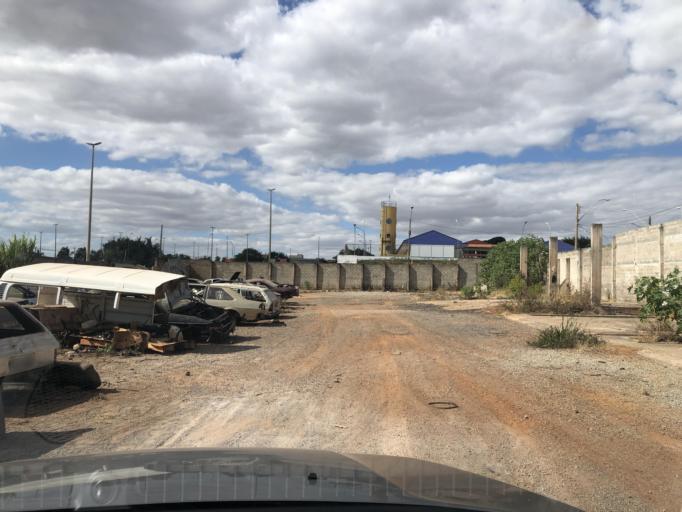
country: BR
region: Federal District
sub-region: Brasilia
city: Brasilia
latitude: -15.8842
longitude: -48.1285
